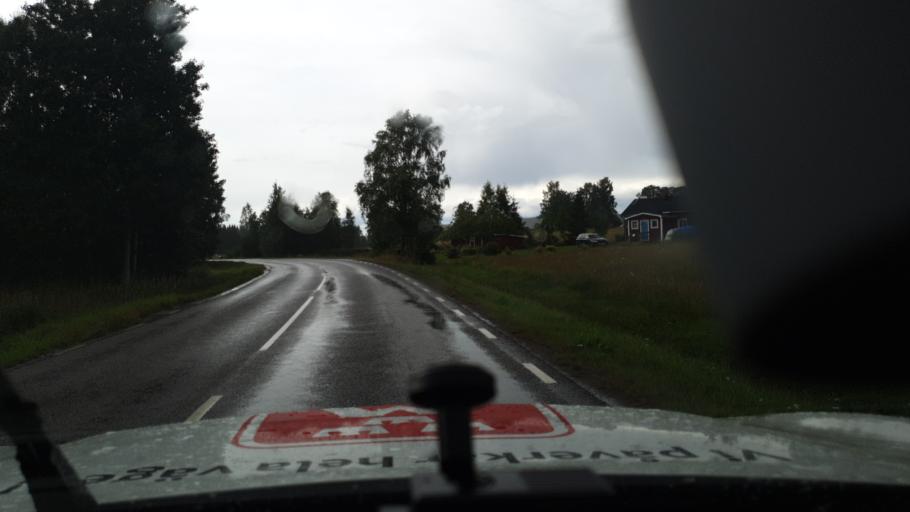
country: SE
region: Vaermland
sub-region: Sunne Kommun
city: Sunne
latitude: 59.7964
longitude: 13.0685
